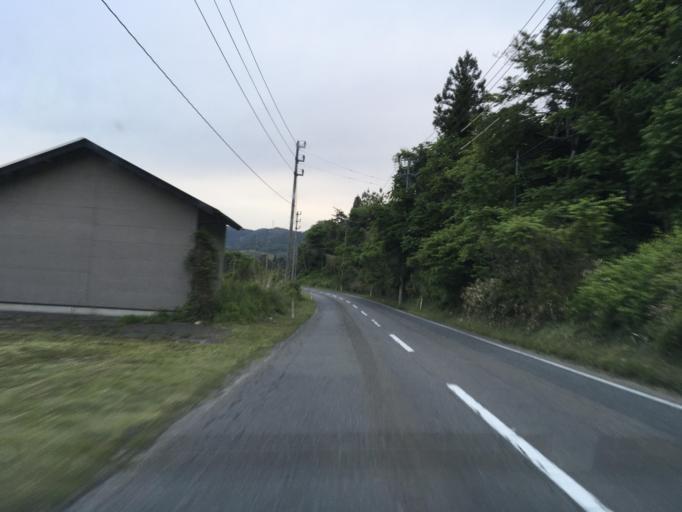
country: JP
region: Iwate
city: Ichinoseki
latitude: 39.0070
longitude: 141.2848
